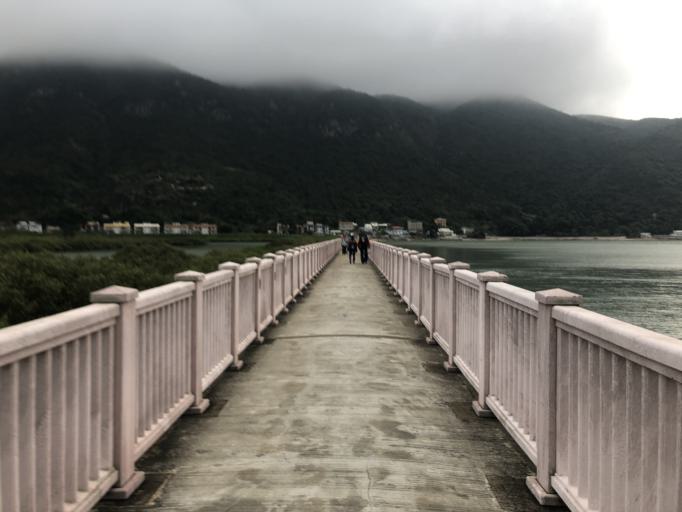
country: HK
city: Tai O
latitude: 22.2507
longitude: 113.8607
